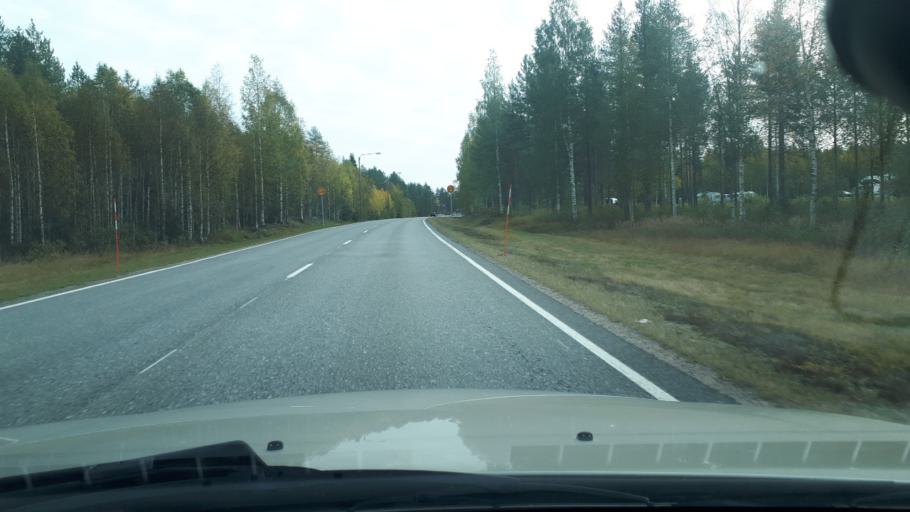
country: FI
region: Lapland
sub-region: Rovaniemi
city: Ranua
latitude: 65.9457
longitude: 26.4587
